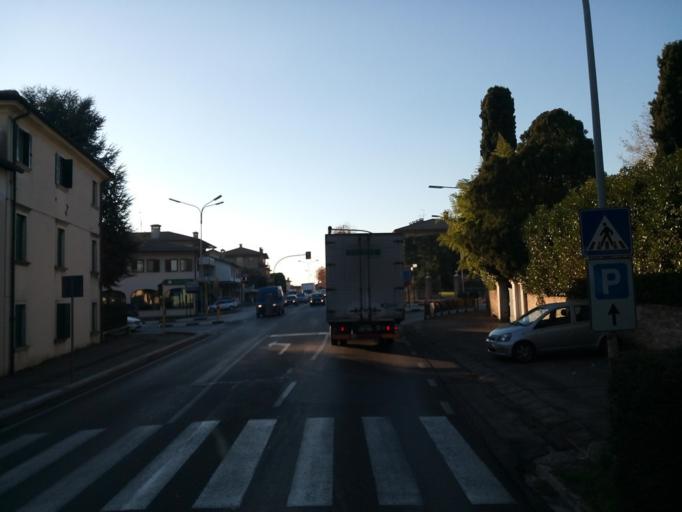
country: IT
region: Veneto
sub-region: Provincia di Treviso
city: Asolo
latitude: 45.7897
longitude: 11.9215
